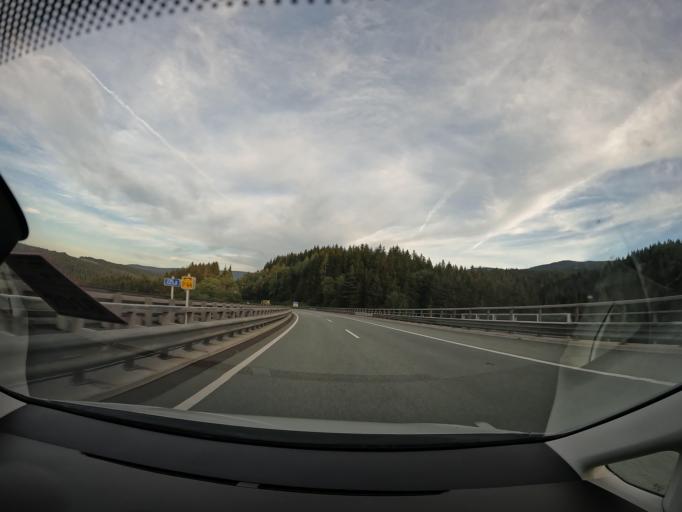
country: AT
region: Styria
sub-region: Politischer Bezirk Voitsberg
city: Modriach
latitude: 46.9557
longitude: 15.0335
